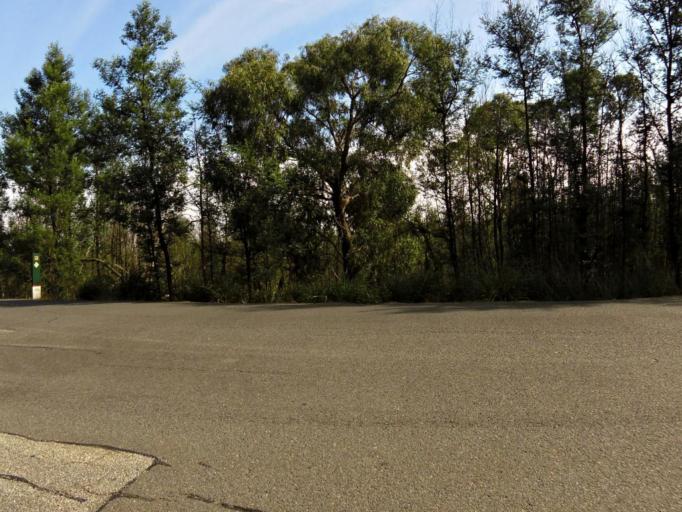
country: AU
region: Victoria
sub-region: Casey
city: Endeavour Hills
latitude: -37.9551
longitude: 145.2553
